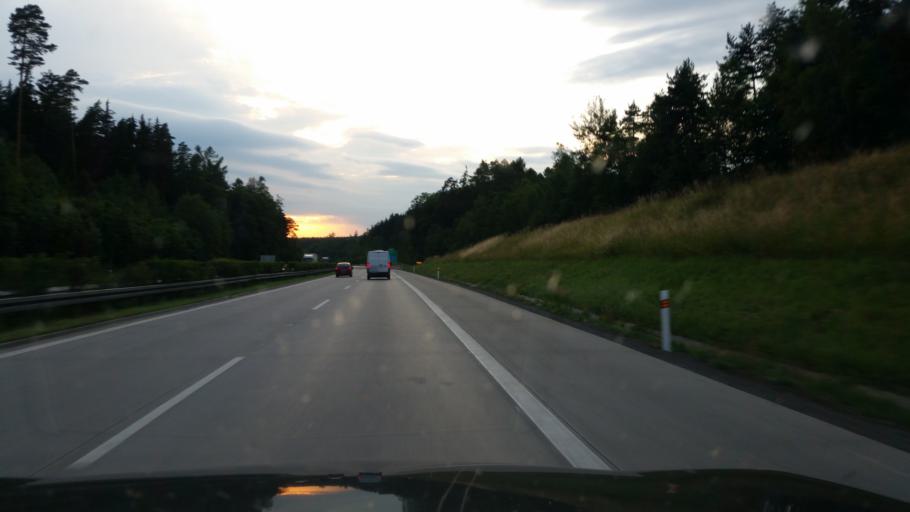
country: CZ
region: Olomoucky
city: Velky Ujezd
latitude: 49.5639
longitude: 17.5062
